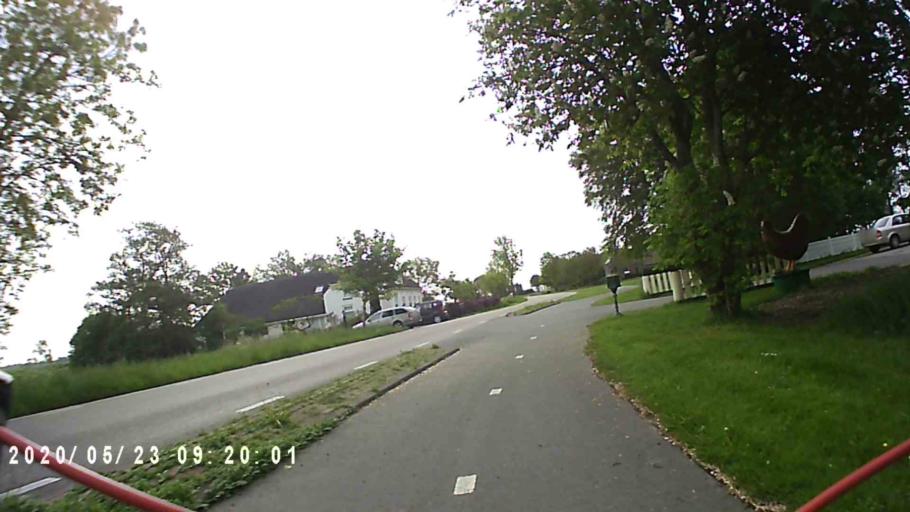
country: NL
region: Groningen
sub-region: Gemeente Bedum
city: Bedum
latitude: 53.2970
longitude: 6.6701
